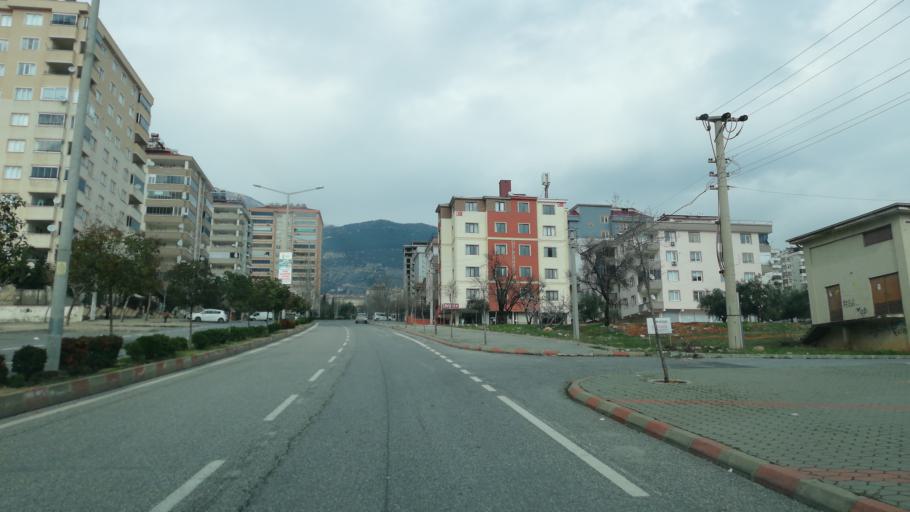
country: TR
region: Kahramanmaras
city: Kahramanmaras
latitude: 37.5898
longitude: 36.8632
